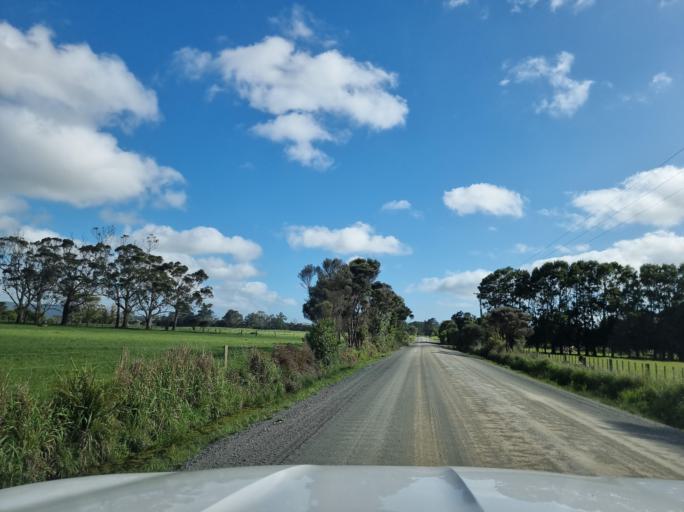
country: NZ
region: Auckland
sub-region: Auckland
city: Wellsford
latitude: -36.1317
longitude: 174.5922
